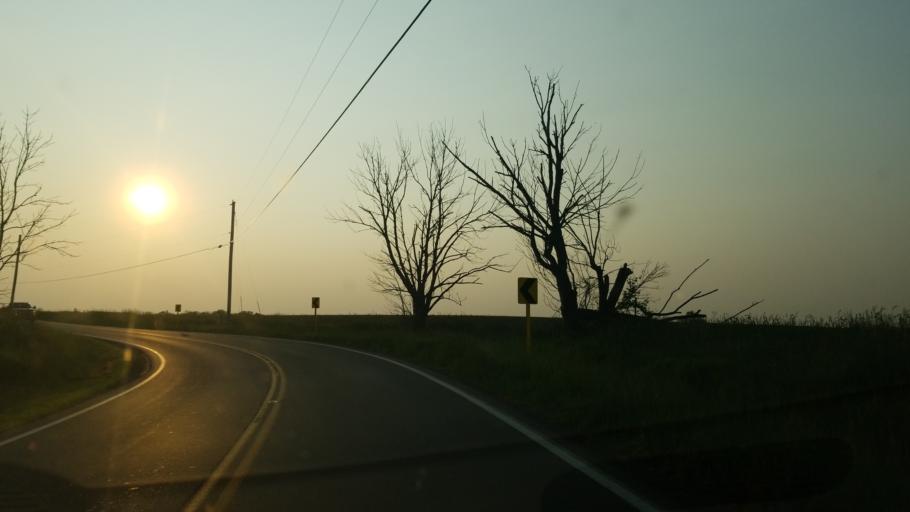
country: US
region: Ohio
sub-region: Ashland County
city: Ashland
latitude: 40.9325
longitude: -82.3025
